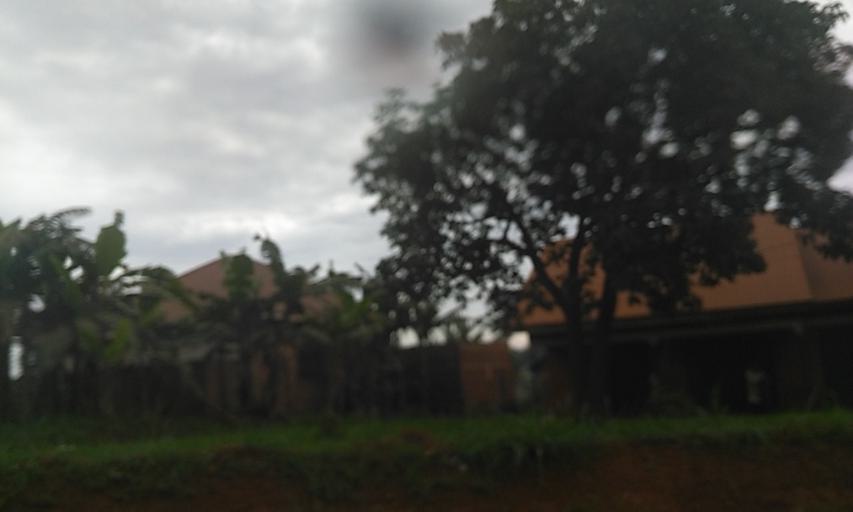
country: UG
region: Central Region
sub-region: Wakiso District
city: Kireka
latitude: 0.4042
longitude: 32.6312
